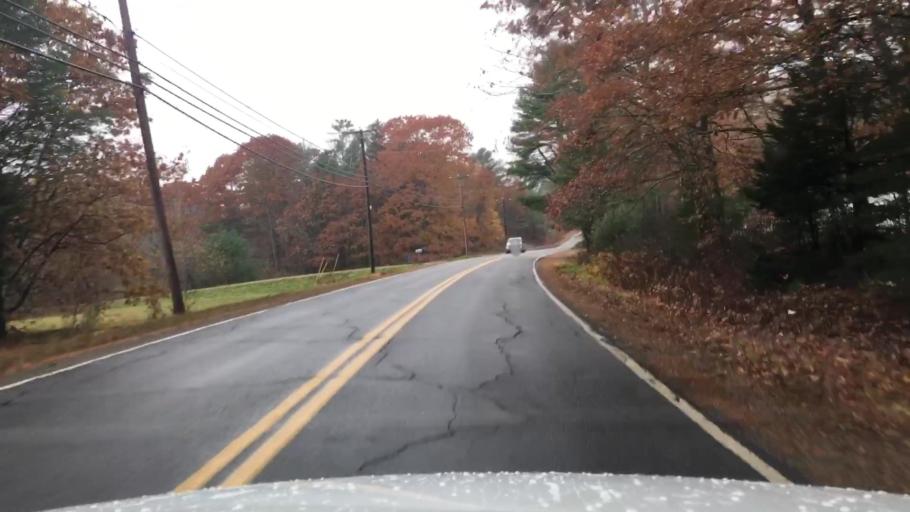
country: US
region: Maine
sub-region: Lincoln County
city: Waldoboro
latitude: 44.0689
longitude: -69.3560
